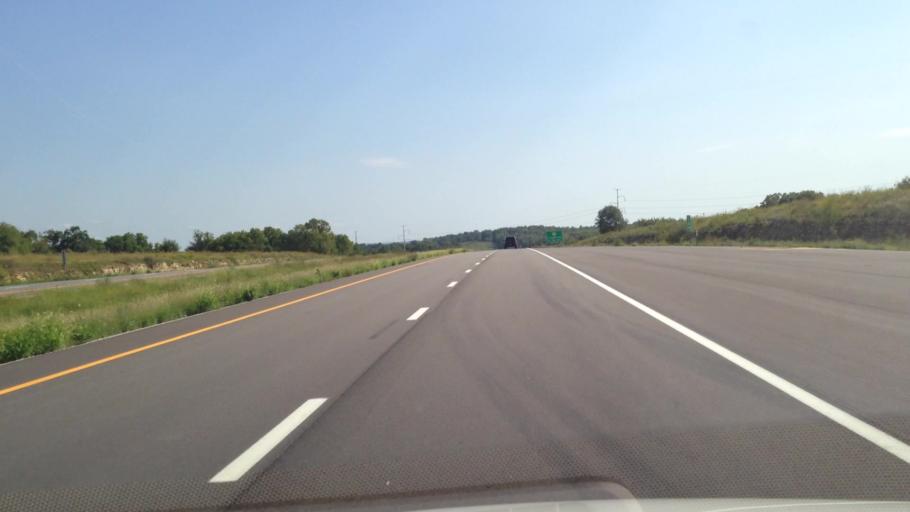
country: US
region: Kansas
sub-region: Linn County
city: La Cygne
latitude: 38.3674
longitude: -94.6877
